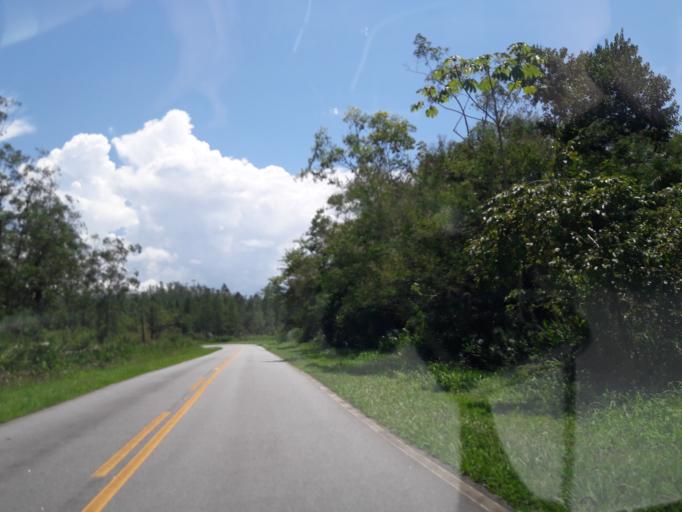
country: BR
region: Parana
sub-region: Antonina
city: Antonina
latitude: -25.5245
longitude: -48.7803
